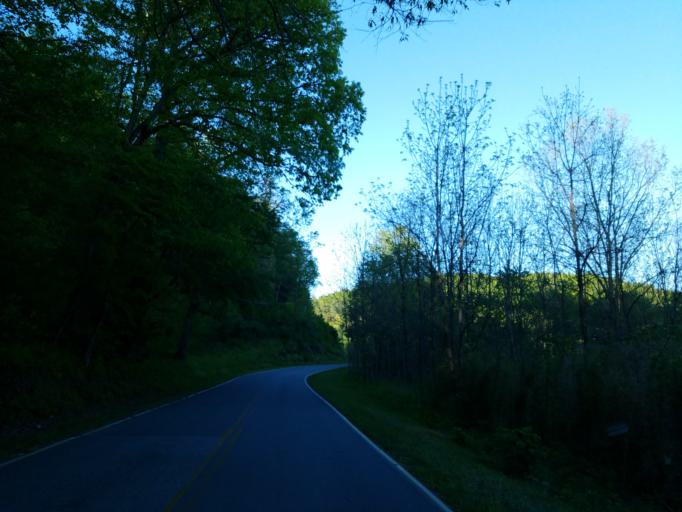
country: US
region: Georgia
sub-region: Fannin County
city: Blue Ridge
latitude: 34.7579
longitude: -84.1985
